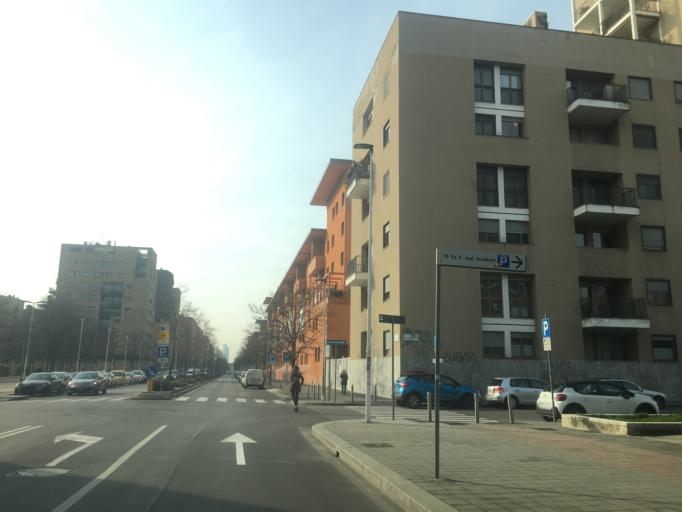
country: IT
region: Lombardy
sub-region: Citta metropolitana di Milano
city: Sesto San Giovanni
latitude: 45.5174
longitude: 9.2122
